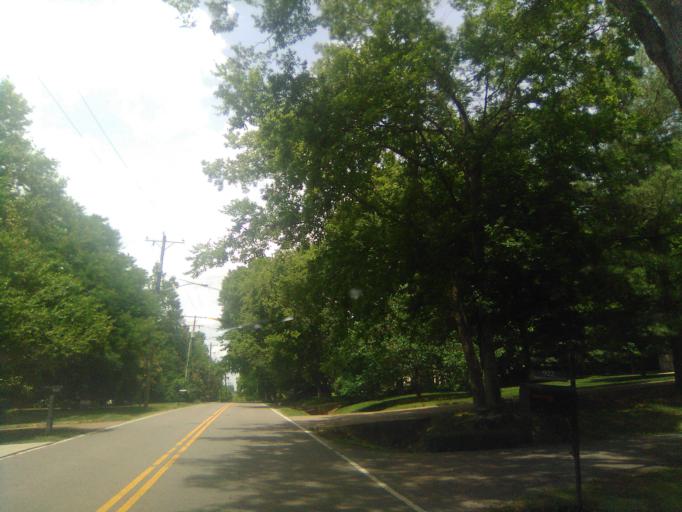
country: US
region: Tennessee
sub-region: Davidson County
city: Belle Meade
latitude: 36.0872
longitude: -86.8515
